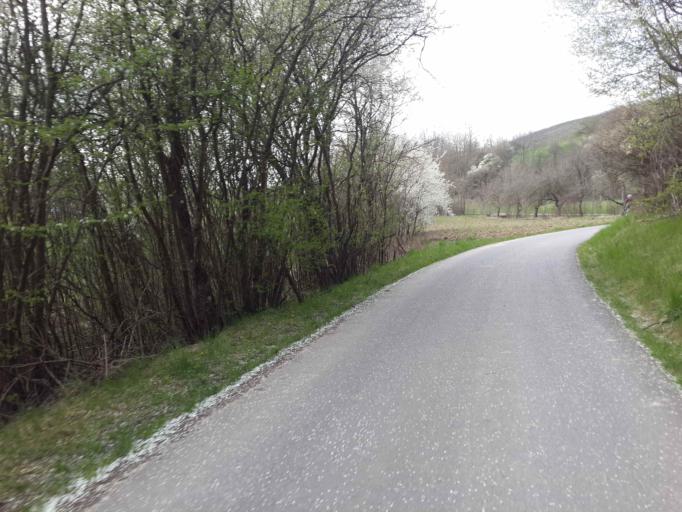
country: DE
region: Baden-Wuerttemberg
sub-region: Regierungsbezirk Stuttgart
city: Dorzbach
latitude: 49.3893
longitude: 9.6816
